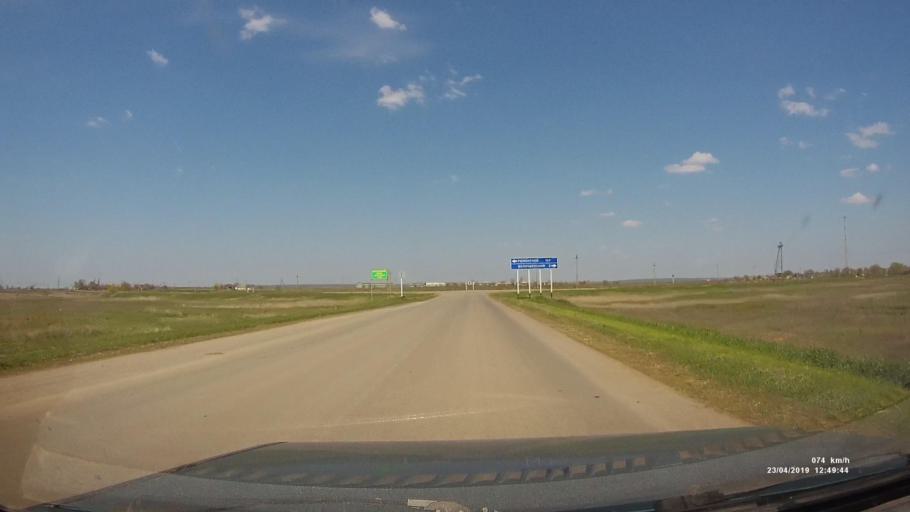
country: RU
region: Kalmykiya
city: Yashalta
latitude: 46.5408
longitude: 42.6405
